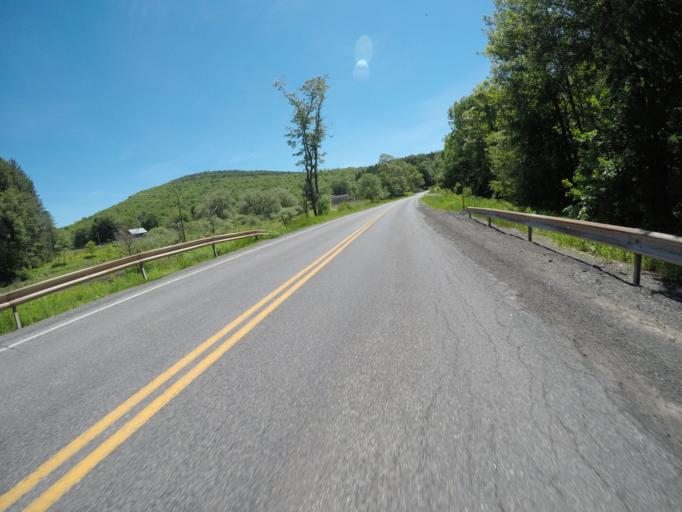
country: US
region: New York
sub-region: Delaware County
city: Delhi
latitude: 42.2154
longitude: -74.8783
